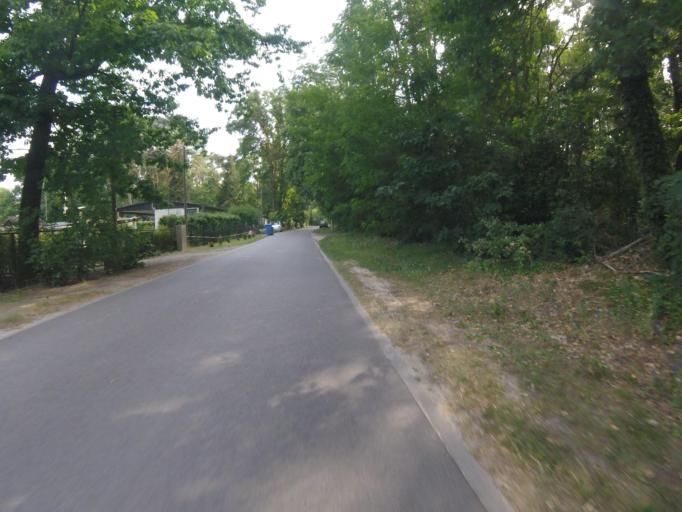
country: DE
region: Brandenburg
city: Spreenhagen
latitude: 52.2697
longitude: 13.8148
